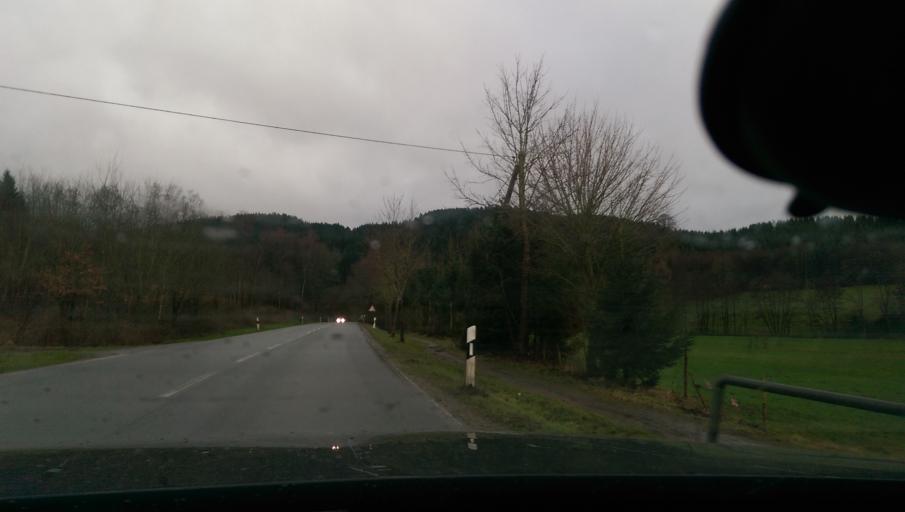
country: DE
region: North Rhine-Westphalia
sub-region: Regierungsbezirk Arnsberg
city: Sundern
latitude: 51.2733
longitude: 7.9503
